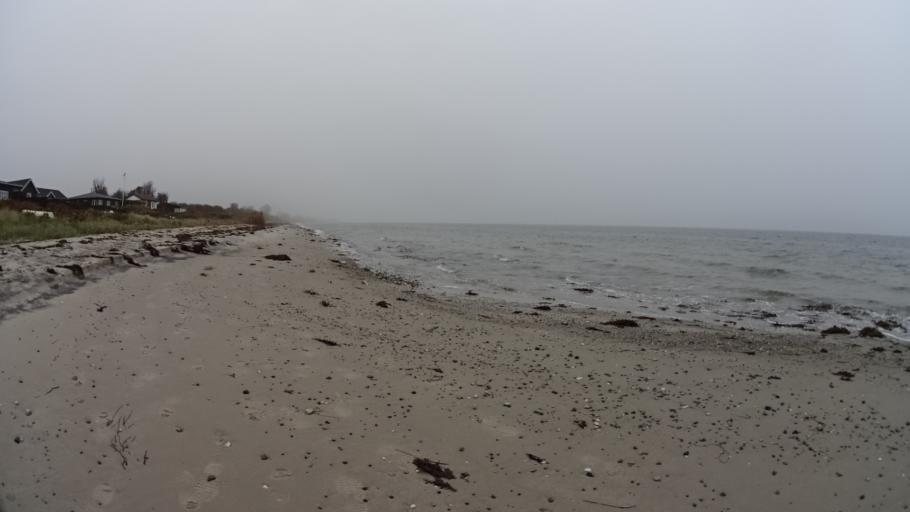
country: DK
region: Central Jutland
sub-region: Odder Kommune
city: Odder
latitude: 55.9395
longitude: 10.2604
